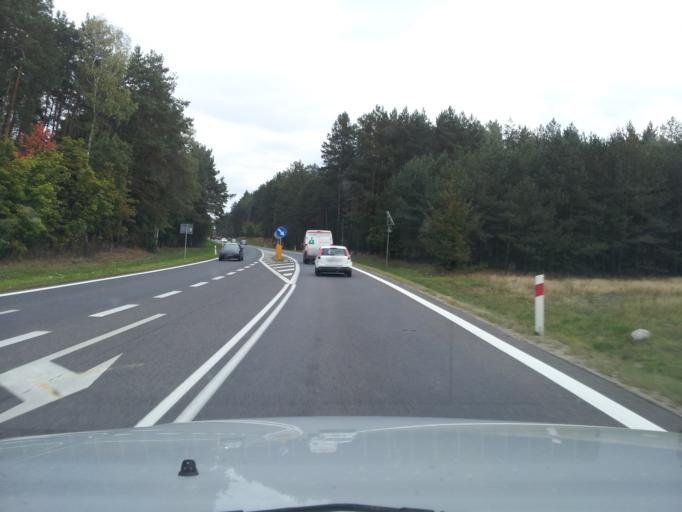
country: PL
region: Warmian-Masurian Voivodeship
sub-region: Powiat olsztynski
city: Gietrzwald
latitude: 53.7533
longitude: 20.2818
